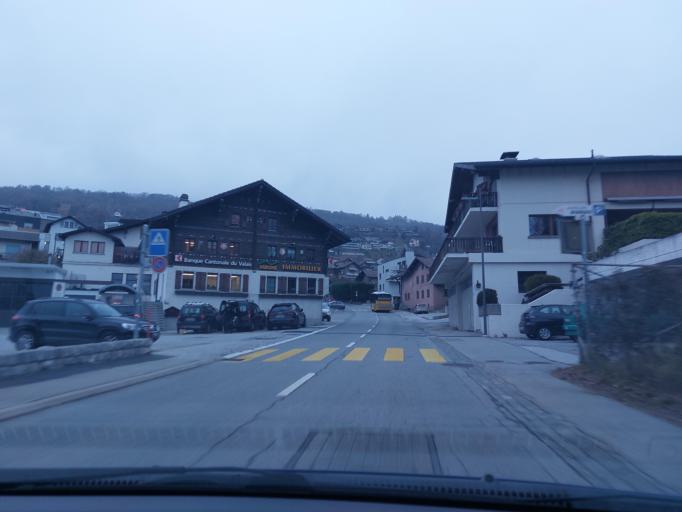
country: CH
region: Valais
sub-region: Sion District
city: Saviese
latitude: 46.2484
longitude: 7.3481
